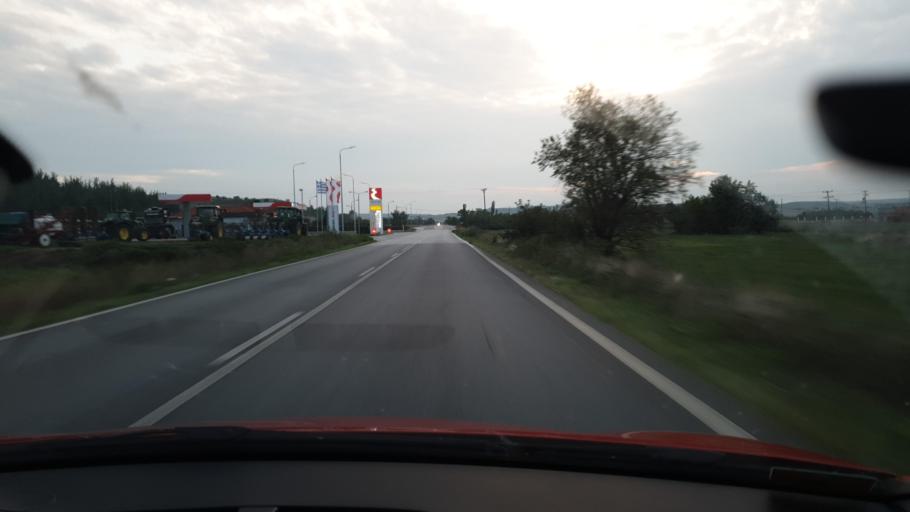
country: GR
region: Central Macedonia
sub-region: Nomos Kilkis
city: Kristoni
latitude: 40.9997
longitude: 22.7715
